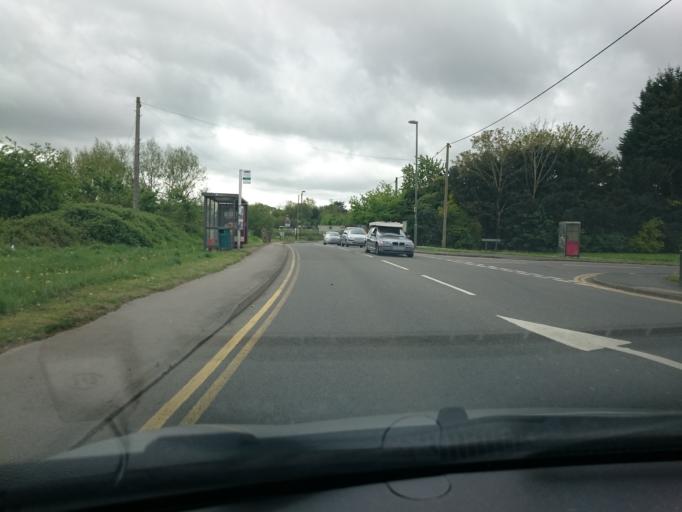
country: GB
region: England
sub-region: Surrey
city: Seale
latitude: 51.2506
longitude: -0.7115
